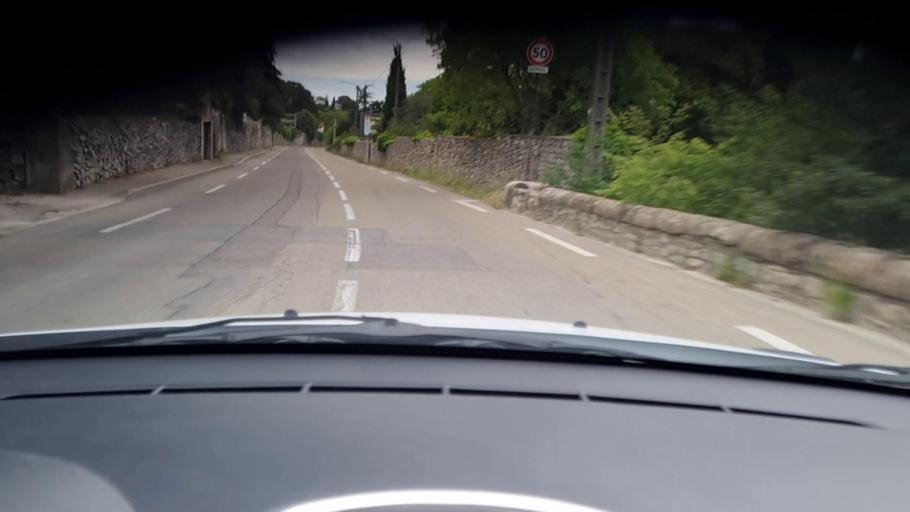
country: FR
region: Languedoc-Roussillon
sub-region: Departement du Gard
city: Nimes
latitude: 43.8615
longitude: 4.3770
